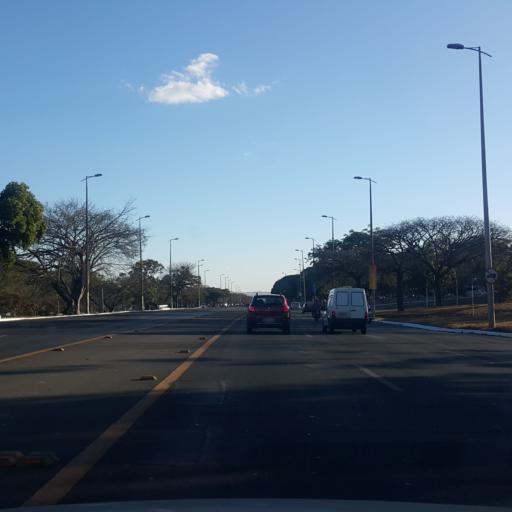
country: BR
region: Federal District
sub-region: Brasilia
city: Brasilia
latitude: -15.8166
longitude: -47.9002
